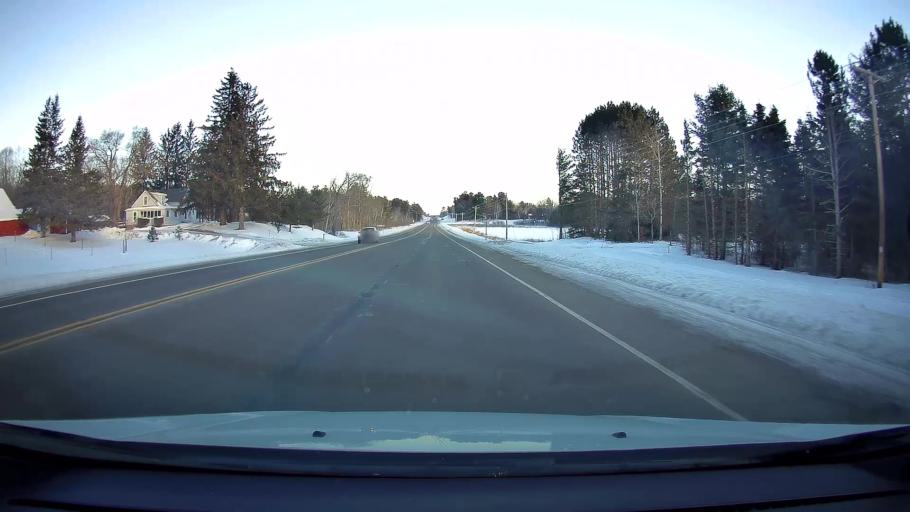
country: US
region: Wisconsin
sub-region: Barron County
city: Cumberland
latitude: 45.5753
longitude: -92.0175
